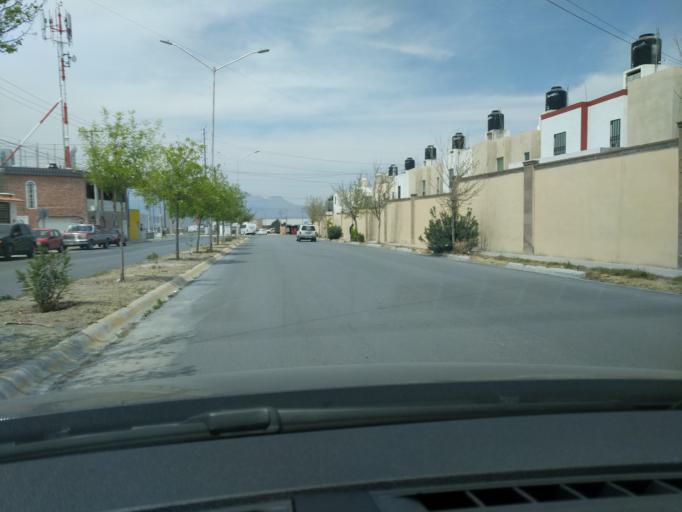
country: MX
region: Coahuila
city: Saltillo
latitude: 25.3570
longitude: -101.0187
